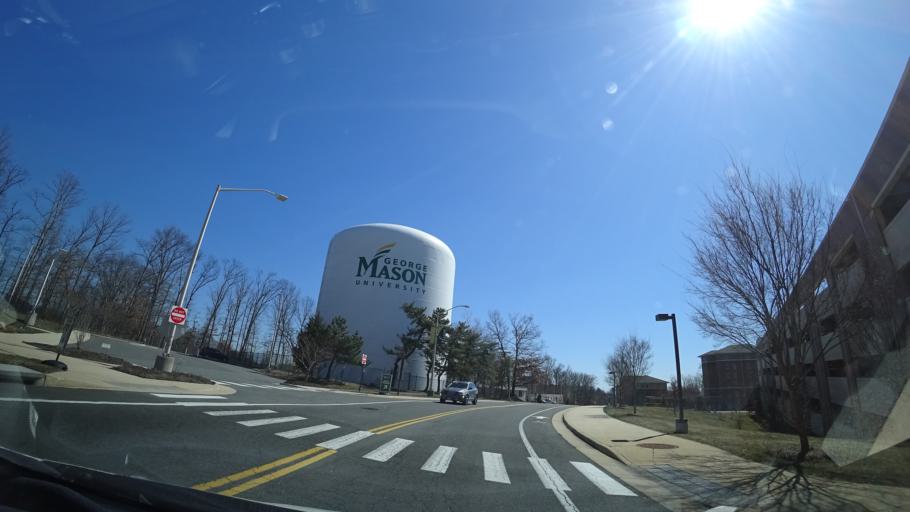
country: US
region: Virginia
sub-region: City of Fairfax
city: Fairfax
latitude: 38.8354
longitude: -77.3050
